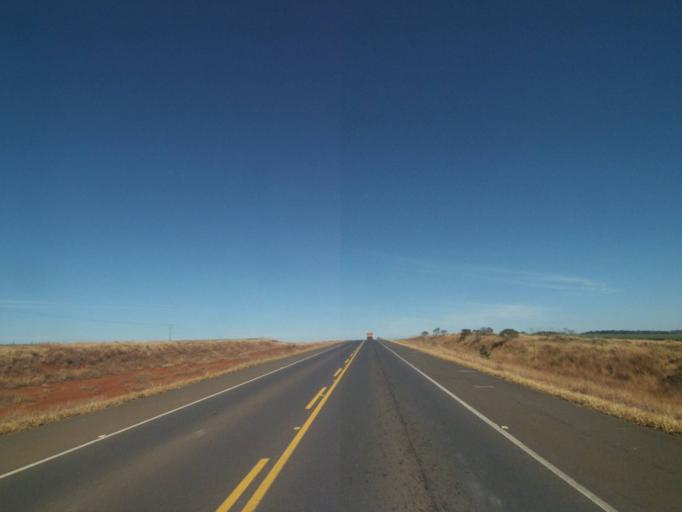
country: BR
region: Parana
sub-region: Tibagi
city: Tibagi
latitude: -24.6235
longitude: -50.4518
